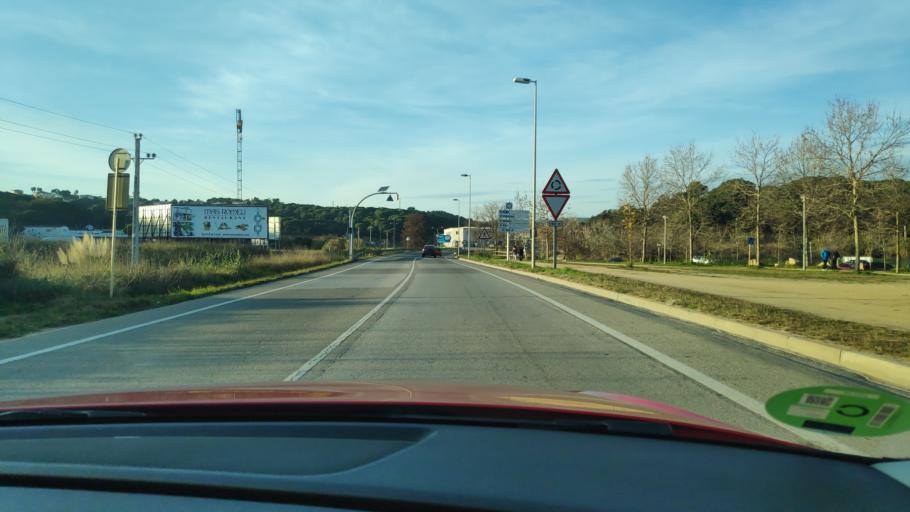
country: ES
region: Catalonia
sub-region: Provincia de Girona
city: Lloret de Mar
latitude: 41.7074
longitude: 2.8341
